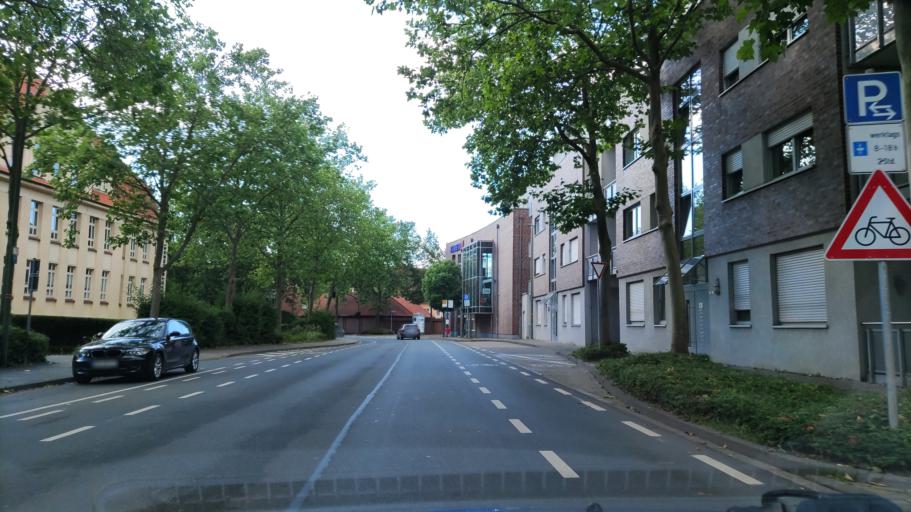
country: DE
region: North Rhine-Westphalia
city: Ahlen
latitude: 51.7613
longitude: 7.8884
